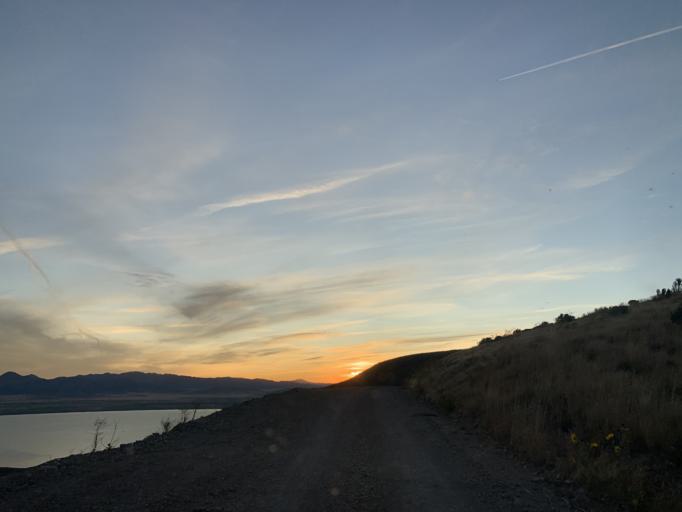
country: US
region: Utah
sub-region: Utah County
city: West Mountain
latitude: 40.1158
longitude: -111.8249
